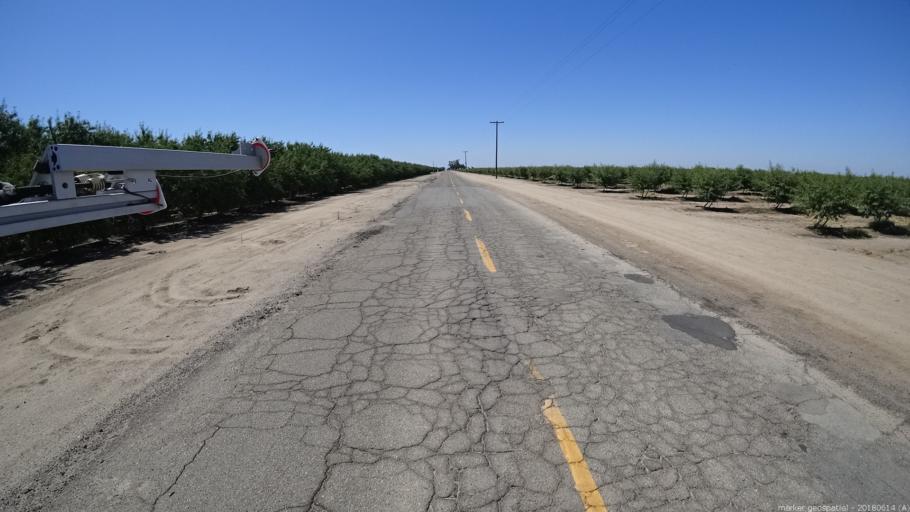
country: US
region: California
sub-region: Madera County
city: Fairmead
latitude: 36.9592
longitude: -120.1840
